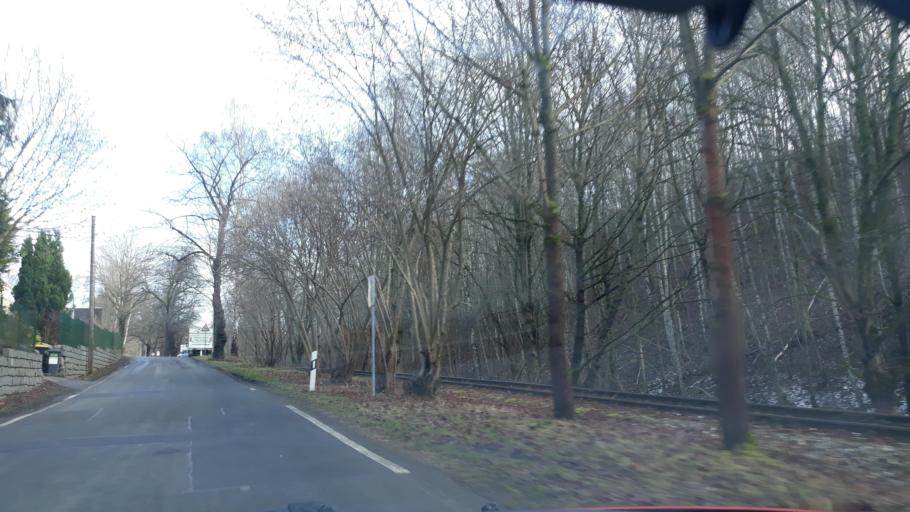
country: DE
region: Saxony
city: Zwickau
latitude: 50.7146
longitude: 12.5180
